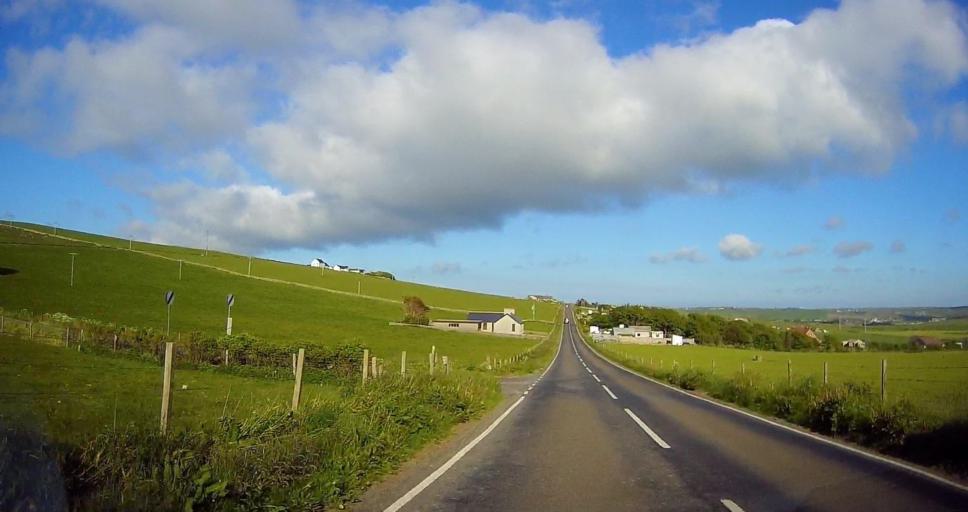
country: GB
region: Scotland
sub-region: Orkney Islands
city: Orkney
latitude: 58.9791
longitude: -3.0226
